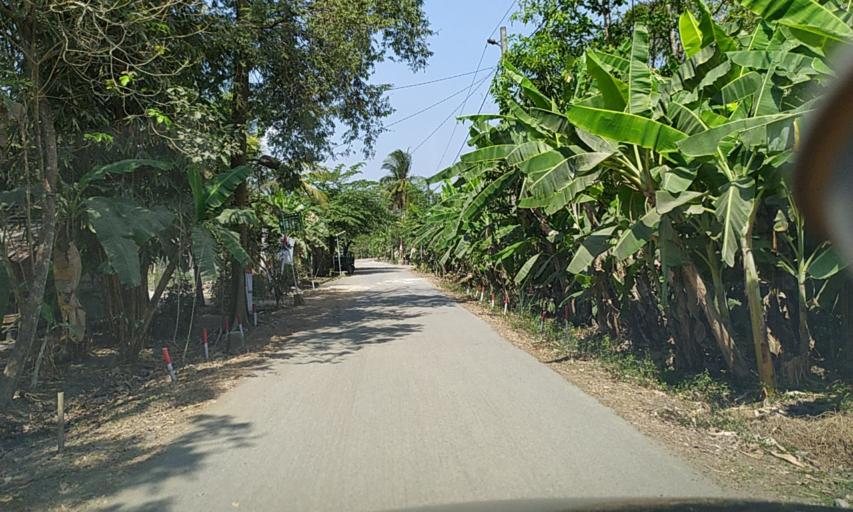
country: ID
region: Central Java
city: Mulyosari
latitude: -7.5025
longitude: 108.7915
